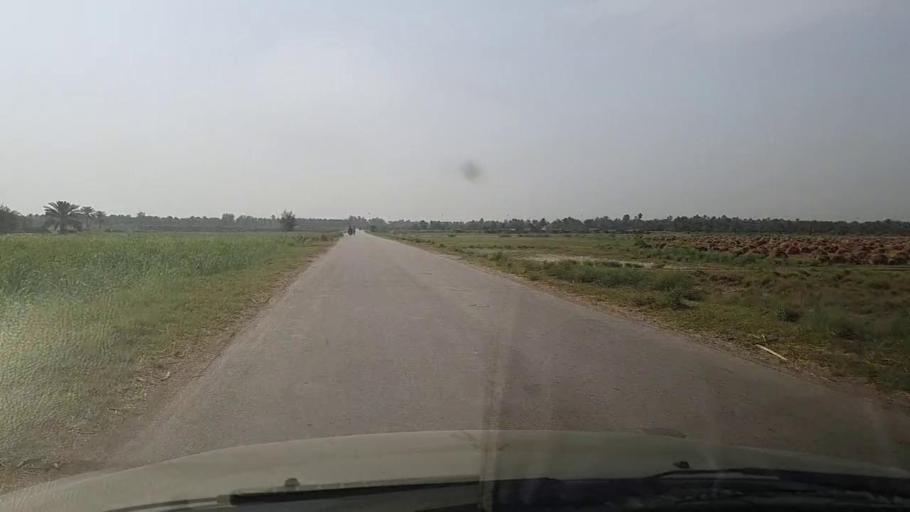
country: PK
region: Sindh
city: Gambat
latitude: 27.4618
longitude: 68.4813
